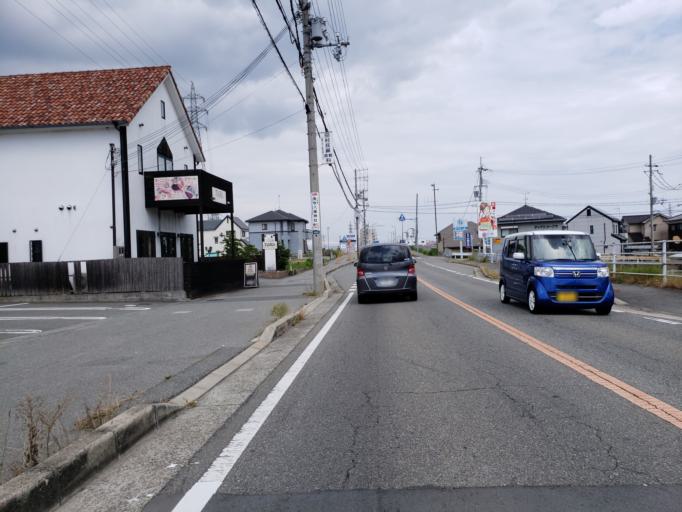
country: JP
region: Hyogo
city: Tatsunocho-tominaga
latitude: 34.7821
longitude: 134.5715
